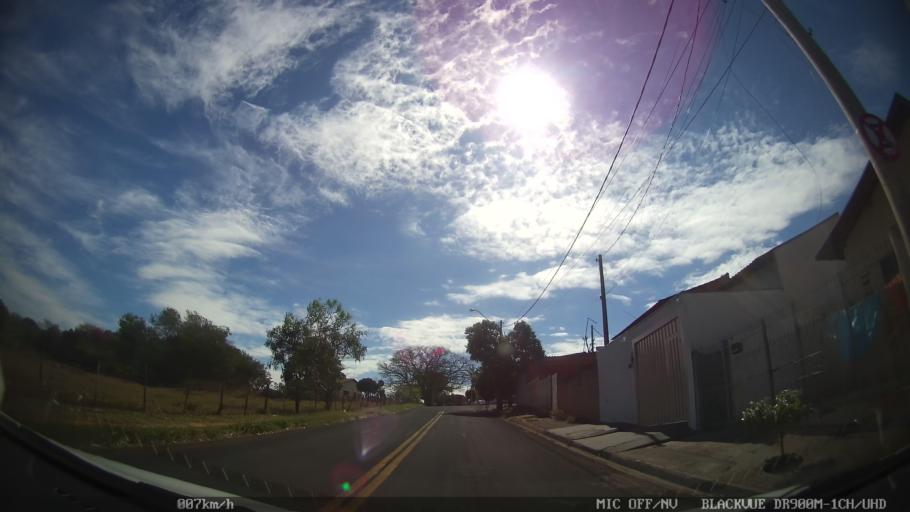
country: BR
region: Sao Paulo
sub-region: Bady Bassitt
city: Bady Bassitt
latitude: -20.8249
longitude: -49.4940
